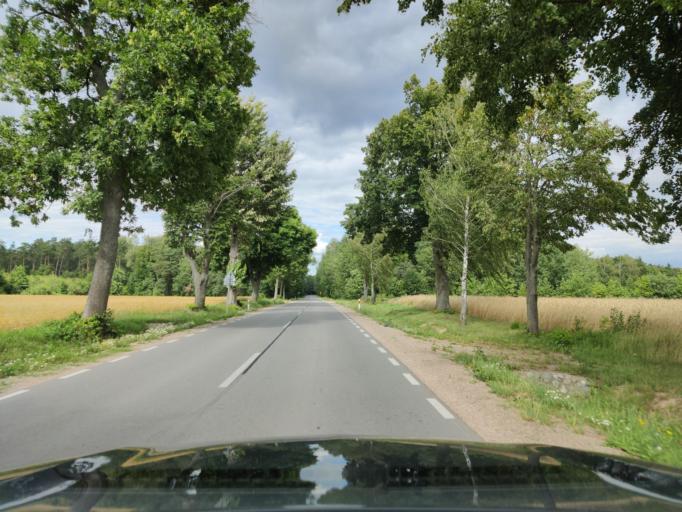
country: PL
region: Masovian Voivodeship
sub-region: Powiat sokolowski
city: Ceranow
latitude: 52.6164
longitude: 22.2059
